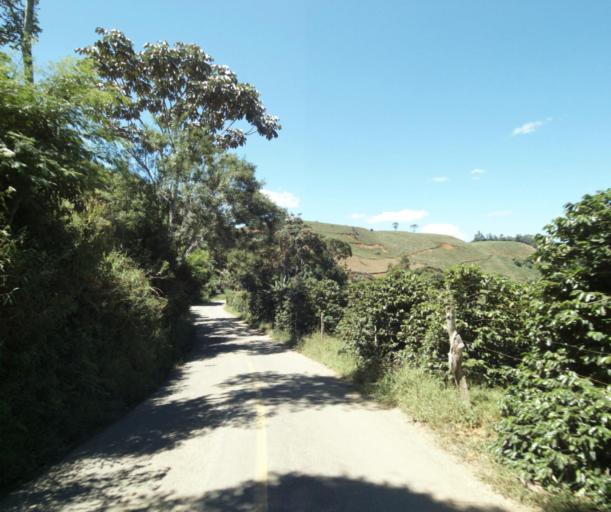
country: BR
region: Minas Gerais
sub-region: Espera Feliz
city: Espera Feliz
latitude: -20.6401
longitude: -41.8094
